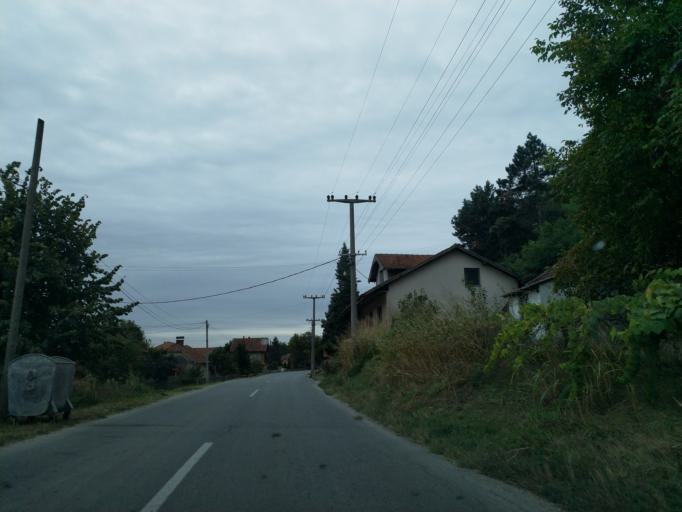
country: RS
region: Central Serbia
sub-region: Sumadijski Okrug
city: Batocina
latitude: 44.1036
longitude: 21.1620
